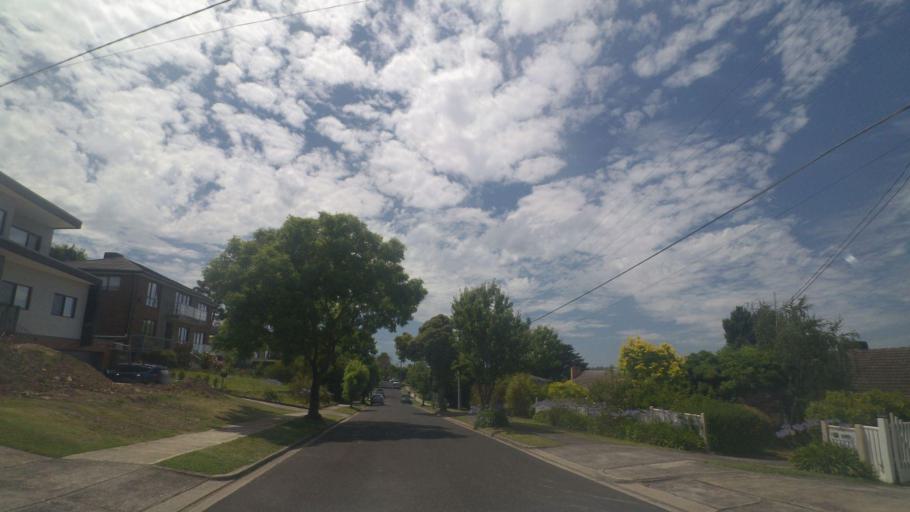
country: AU
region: Victoria
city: Rosanna
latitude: -37.7479
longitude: 145.0754
